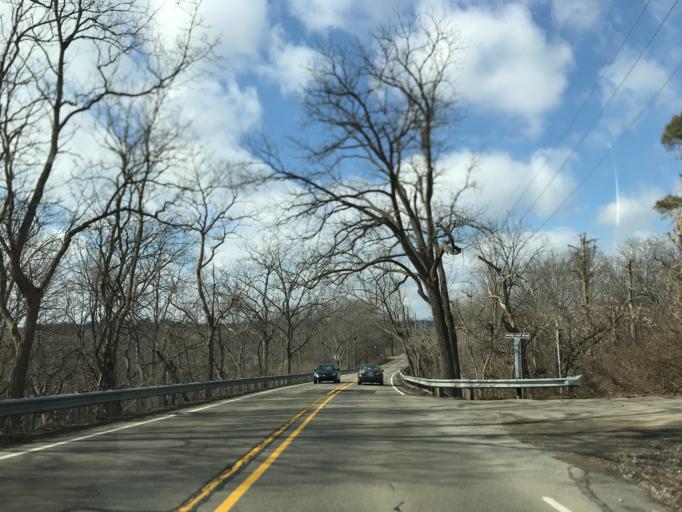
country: US
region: Michigan
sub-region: Washtenaw County
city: Ann Arbor
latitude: 42.2767
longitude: -83.6922
